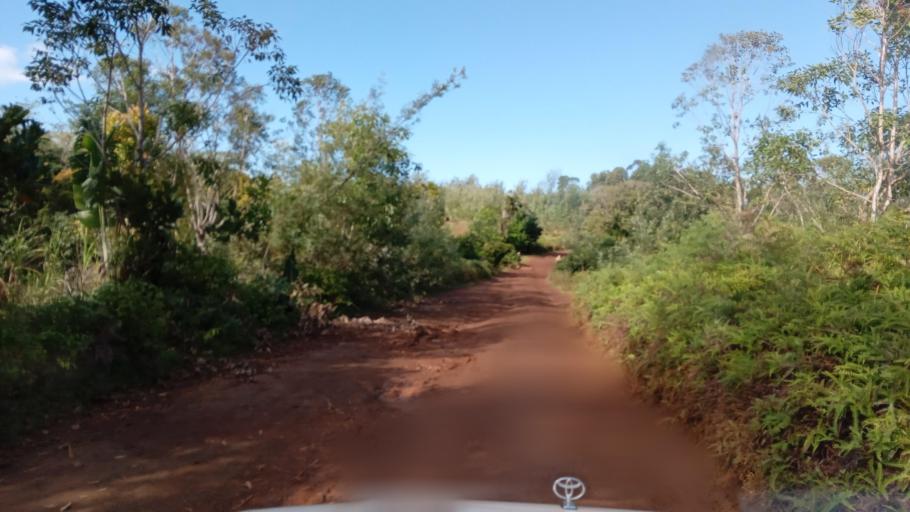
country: MG
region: Atsimo-Atsinanana
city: Vohipaho
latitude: -23.6574
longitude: 47.5838
